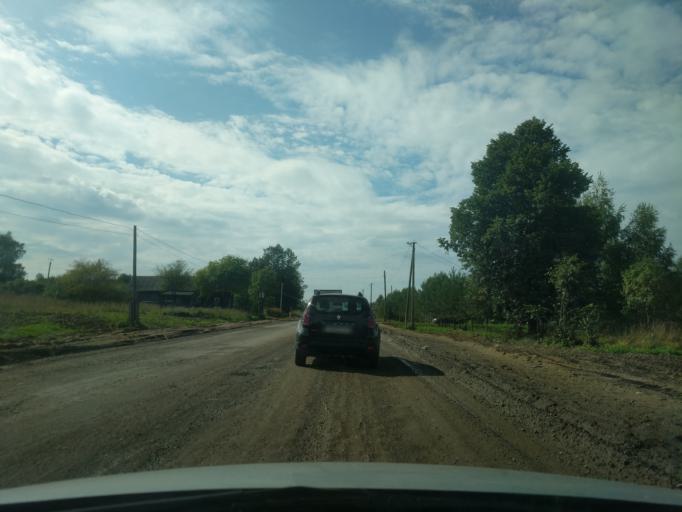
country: RU
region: Kostroma
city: Sudislavl'
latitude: 57.8717
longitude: 41.6536
